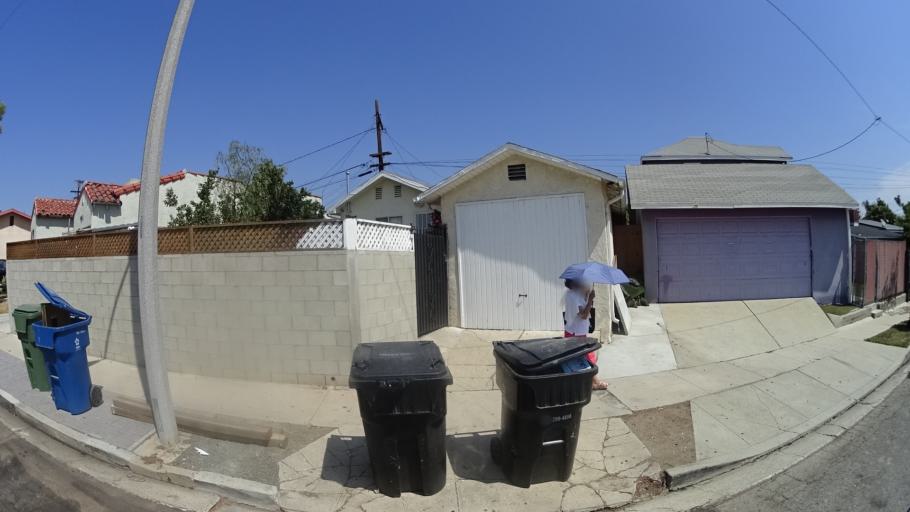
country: US
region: California
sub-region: Los Angeles County
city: View Park-Windsor Hills
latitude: 33.9804
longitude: -118.3425
